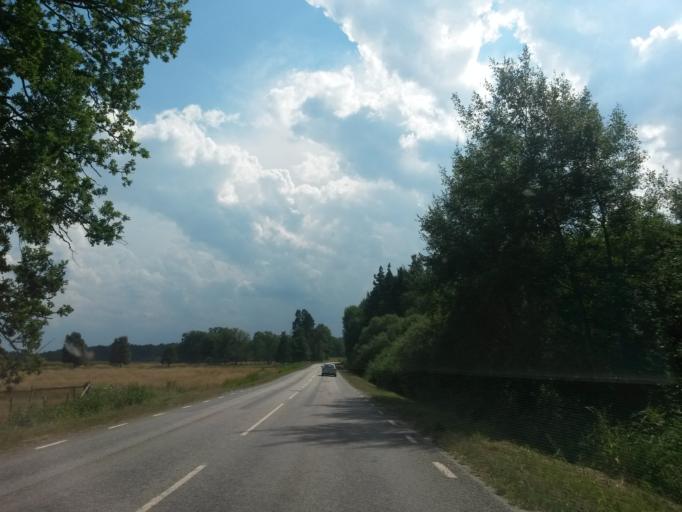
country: SE
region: Vaestra Goetaland
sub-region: Lidkopings Kommun
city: Lidkoping
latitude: 58.6318
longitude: 13.1384
